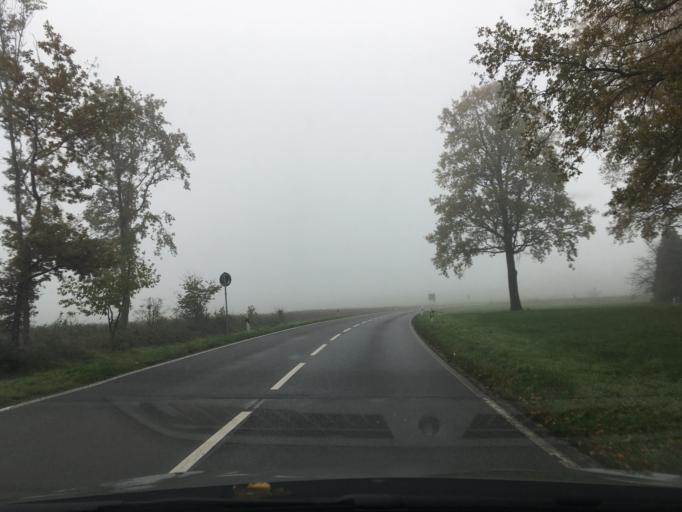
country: DE
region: North Rhine-Westphalia
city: Stadtlohn
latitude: 52.0626
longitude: 6.9346
